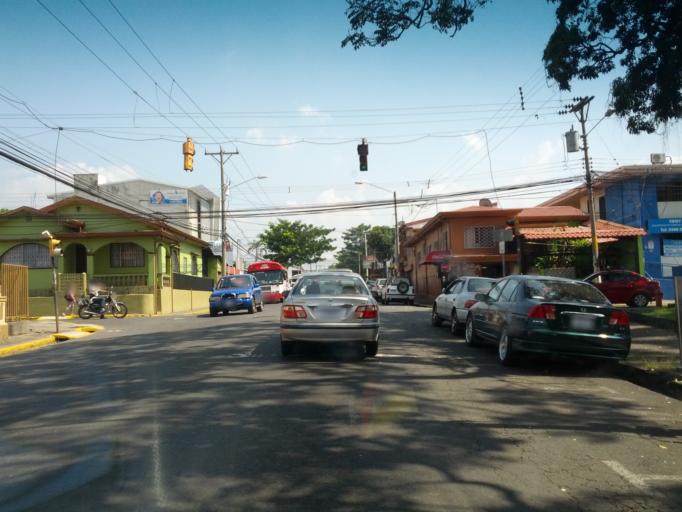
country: CR
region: Alajuela
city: Alajuela
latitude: 10.0206
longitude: -84.2139
